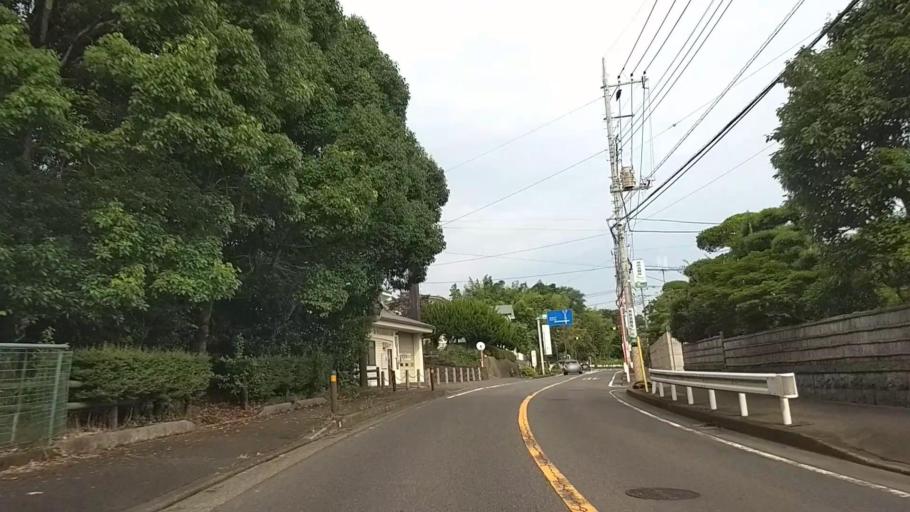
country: JP
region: Kanagawa
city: Oiso
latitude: 35.3284
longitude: 139.3116
